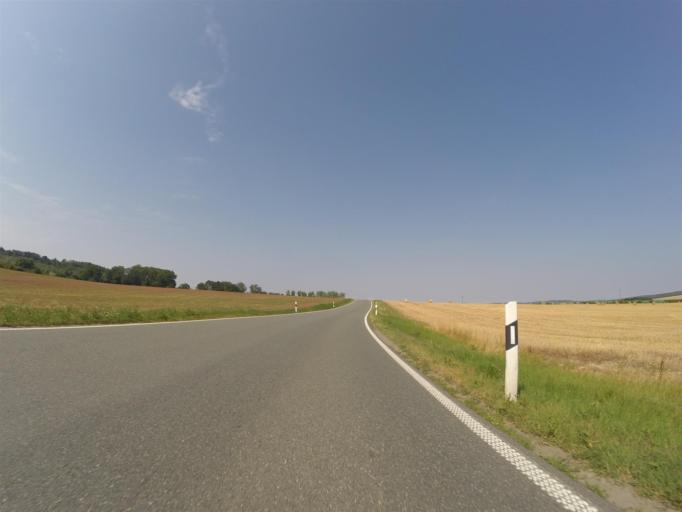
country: DE
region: Thuringia
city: Schongleina
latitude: 50.9160
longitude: 11.7308
